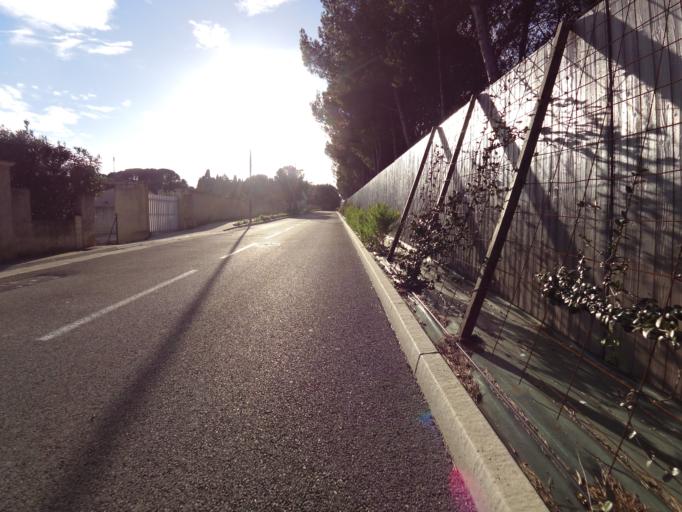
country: FR
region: Languedoc-Roussillon
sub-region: Departement du Gard
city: Aigues-Vives
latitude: 43.7253
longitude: 4.1767
